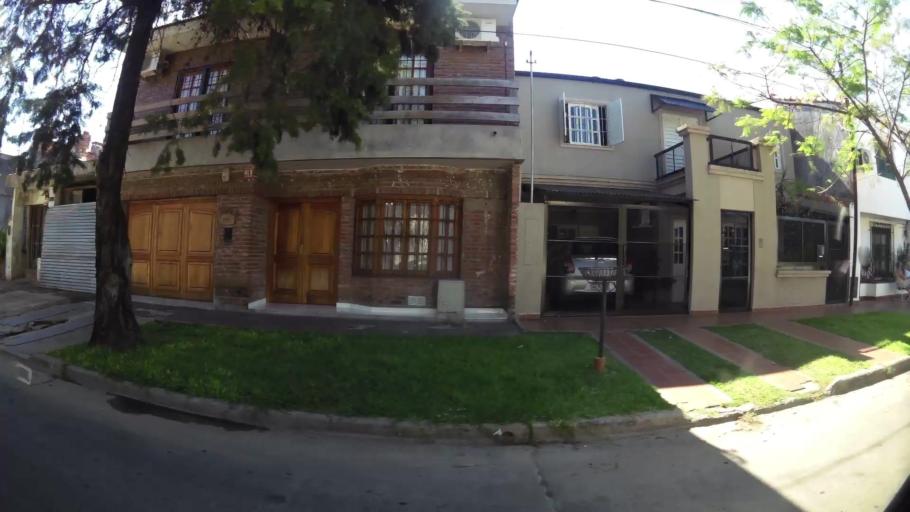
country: AR
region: Santa Fe
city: Santa Fe de la Vera Cruz
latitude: -31.6131
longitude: -60.6782
